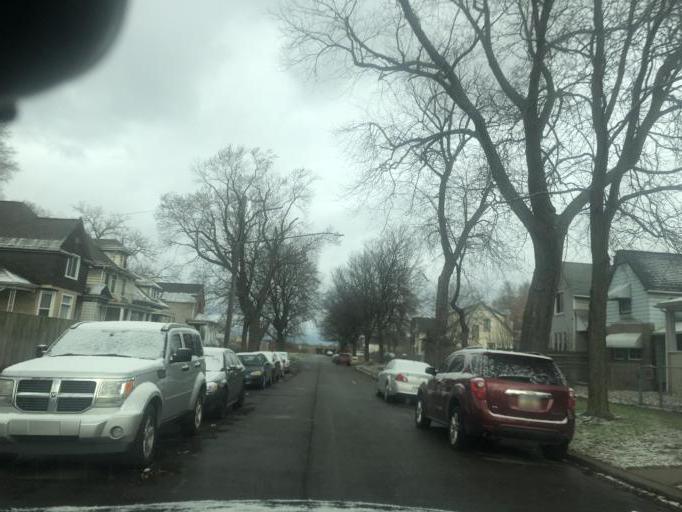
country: US
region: Michigan
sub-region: Wayne County
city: River Rouge
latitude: 42.3131
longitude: -83.1113
